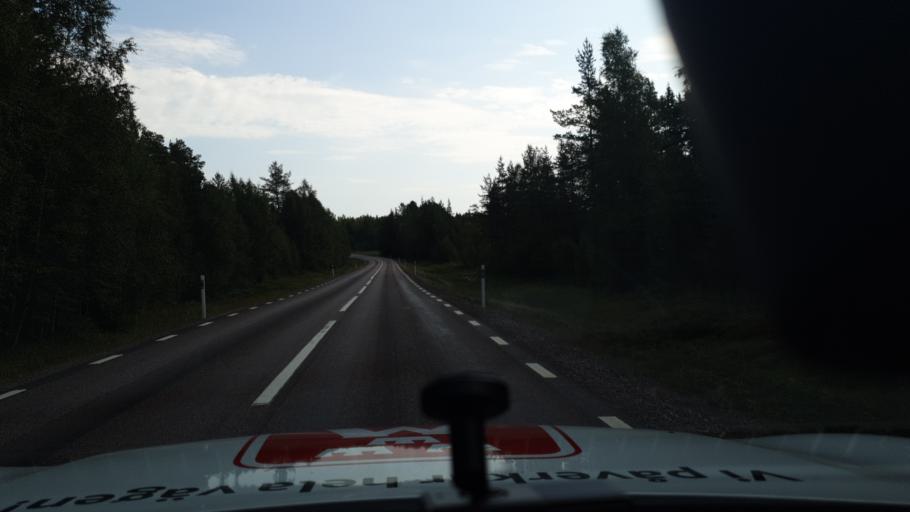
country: SE
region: Vaermland
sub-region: Hagfors Kommun
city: Ekshaerad
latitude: 60.4824
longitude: 13.3956
